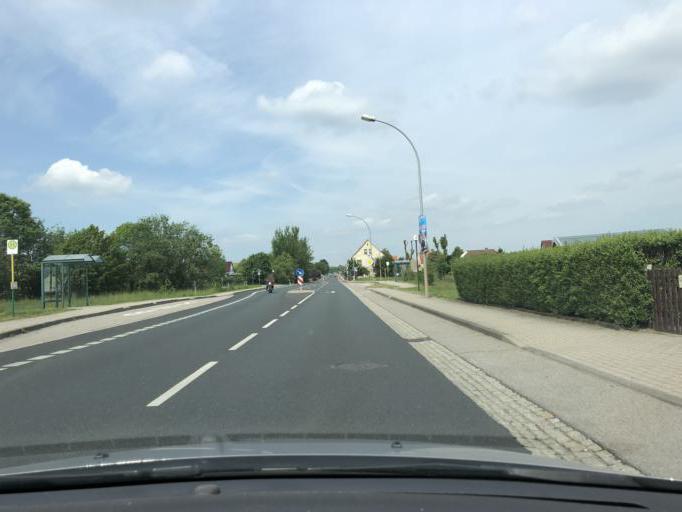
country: DE
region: Thuringia
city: Saara
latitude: 50.9518
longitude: 12.4267
